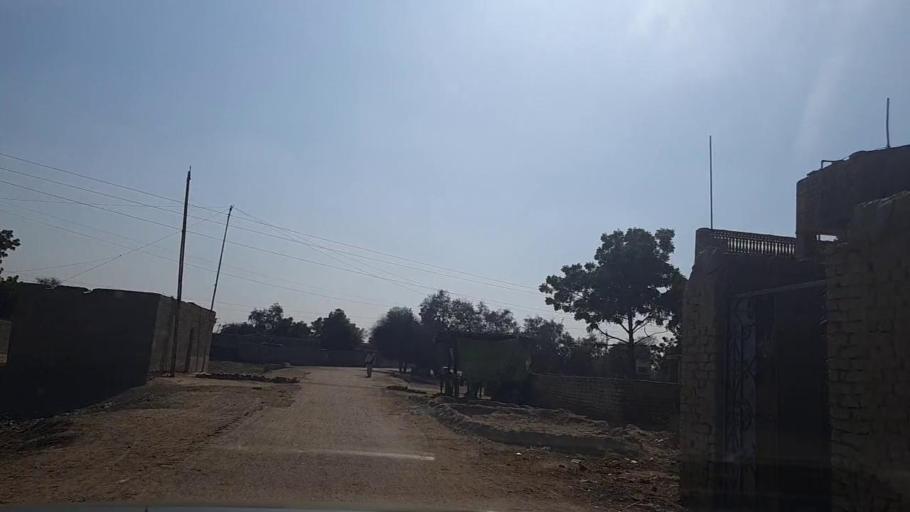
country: PK
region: Sindh
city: Sehwan
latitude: 26.2761
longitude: 68.0363
